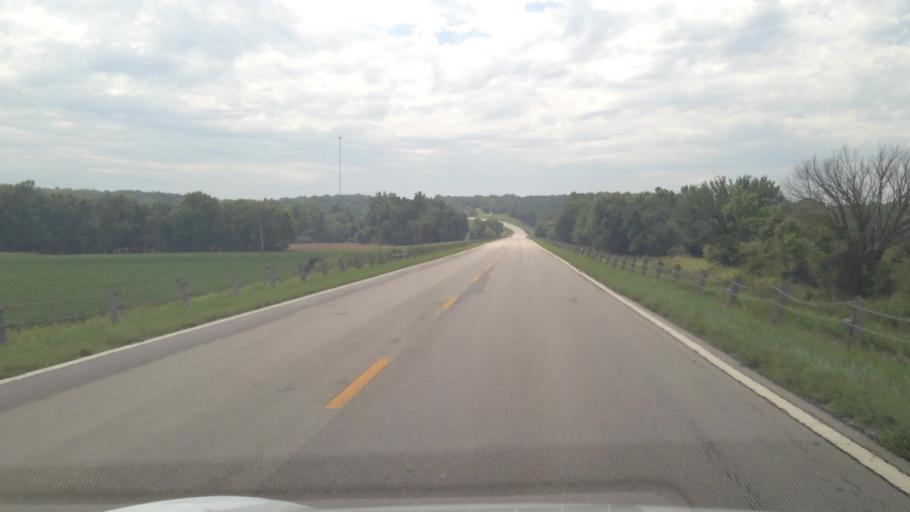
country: US
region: Kansas
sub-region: Bourbon County
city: Fort Scott
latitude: 37.8406
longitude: -94.9813
